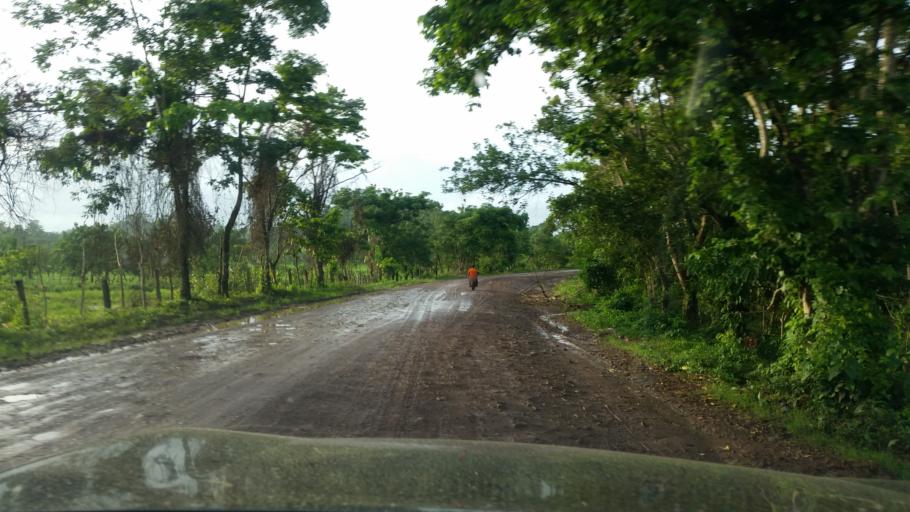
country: NI
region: Atlantico Norte (RAAN)
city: Siuna
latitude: 13.3555
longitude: -84.8891
